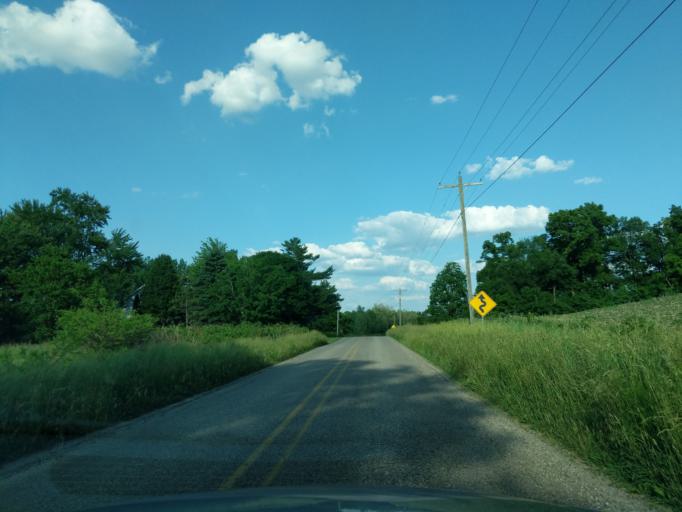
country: US
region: Indiana
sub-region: Kosciusko County
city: North Webster
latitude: 41.3025
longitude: -85.5934
